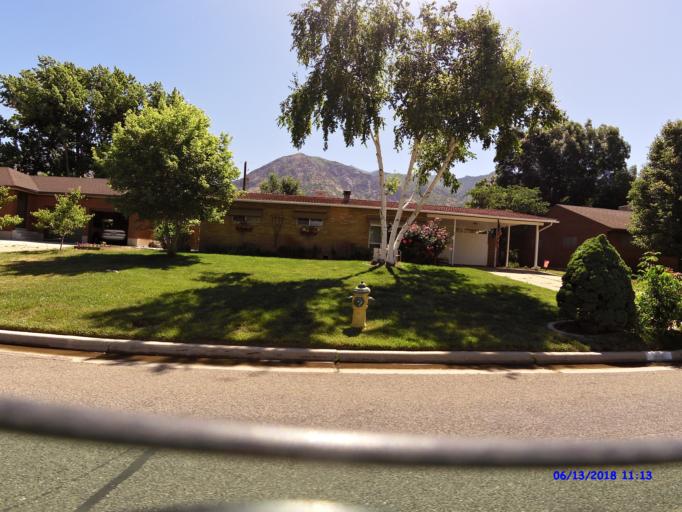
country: US
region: Utah
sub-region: Weber County
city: South Ogden
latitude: 41.2070
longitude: -111.9473
